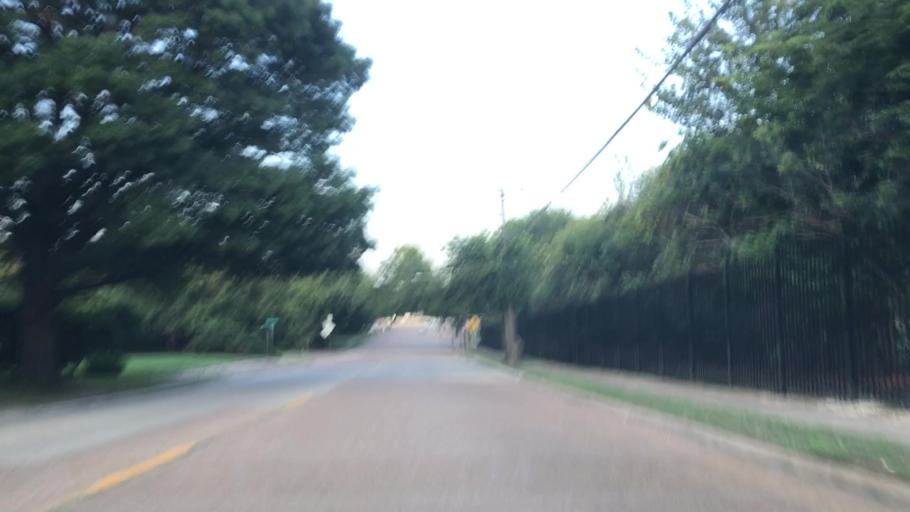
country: US
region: Texas
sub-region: Dallas County
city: University Park
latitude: 32.9013
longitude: -96.7729
